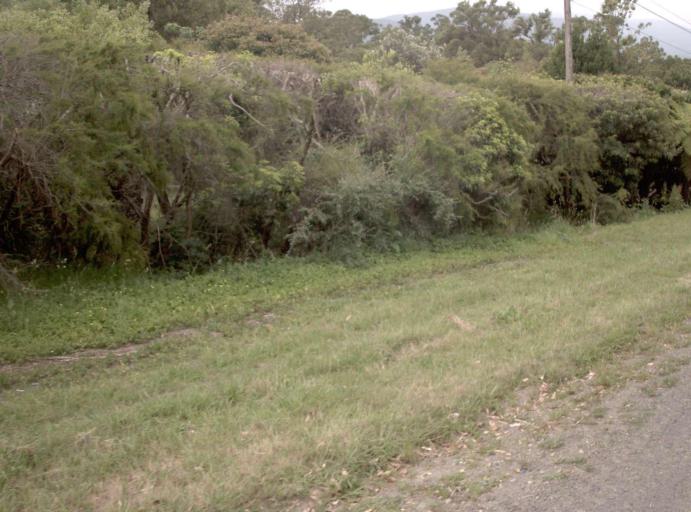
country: AU
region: Victoria
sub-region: Yarra Ranges
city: Woori Yallock
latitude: -37.7755
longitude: 145.4983
